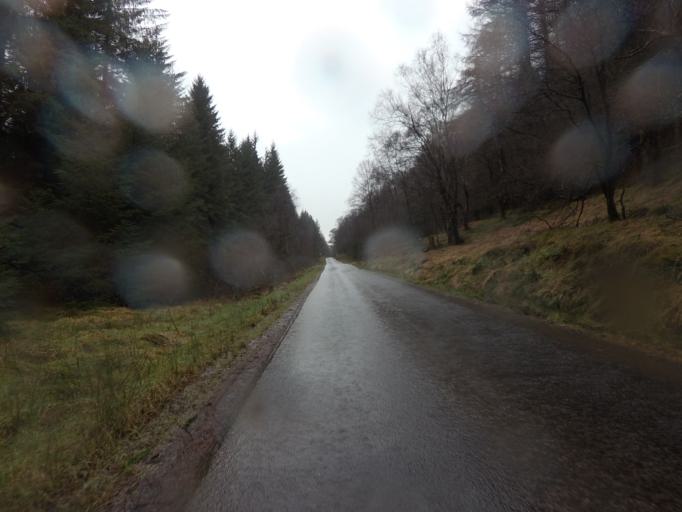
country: GB
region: Scotland
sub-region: West Dunbartonshire
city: Balloch
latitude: 56.2303
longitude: -4.5571
